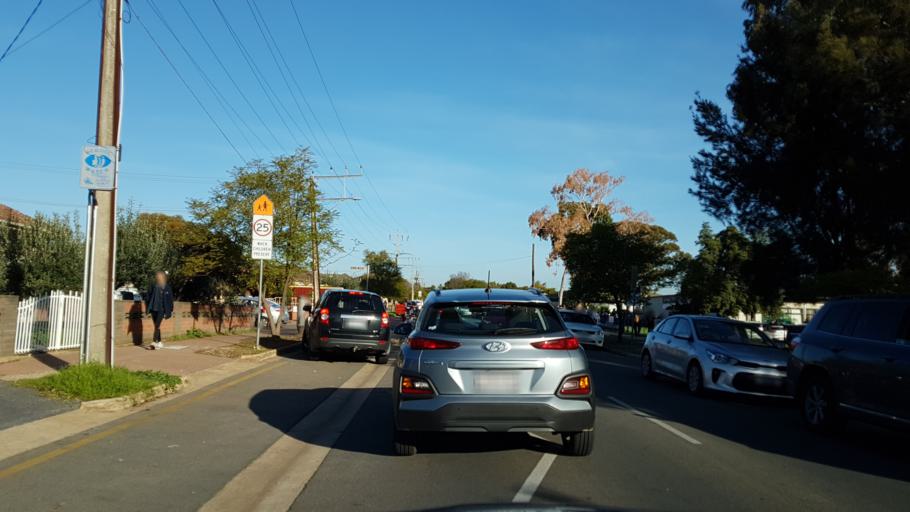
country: AU
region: South Australia
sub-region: Campbelltown
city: Campbelltown
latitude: -34.8894
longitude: 138.6678
